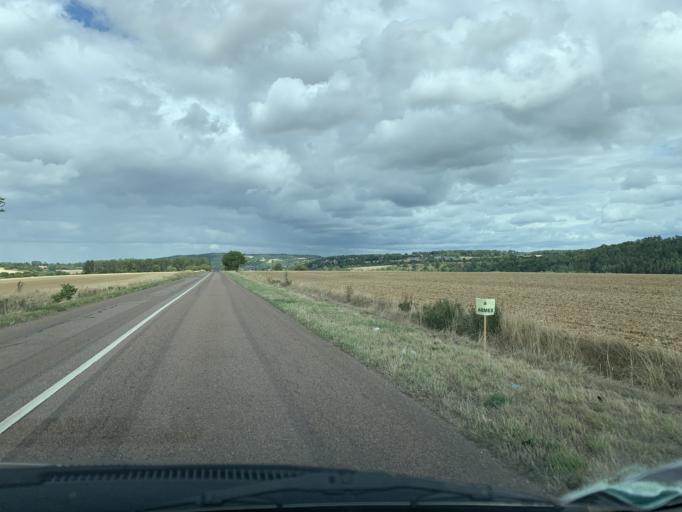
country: FR
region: Bourgogne
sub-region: Departement de la Nievre
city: Clamecy
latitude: 47.4409
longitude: 3.4925
